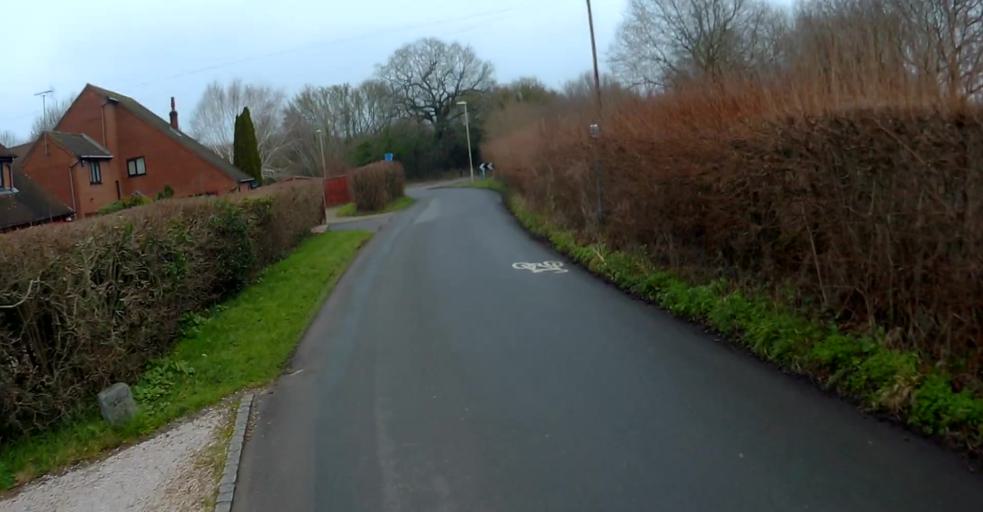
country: GB
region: England
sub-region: Hampshire
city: Old Basing
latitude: 51.2774
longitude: -1.0517
